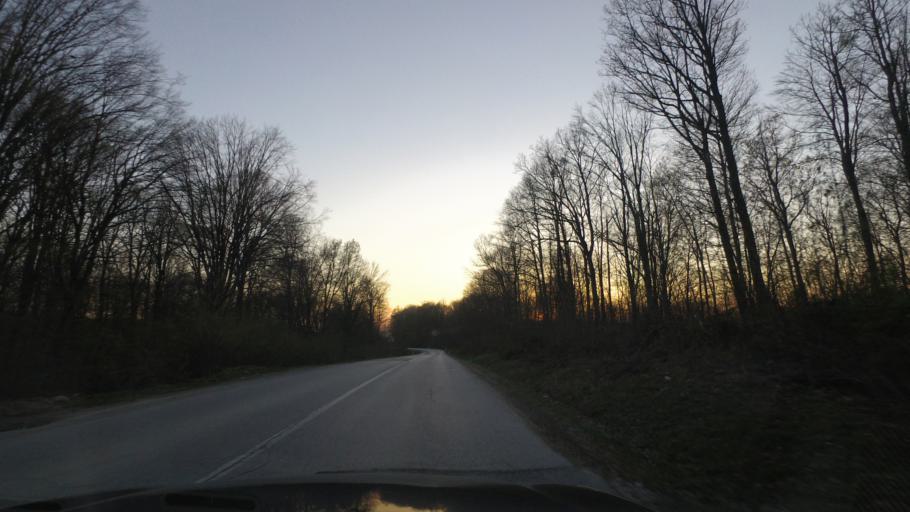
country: HR
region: Karlovacka
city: Vojnic
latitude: 45.3440
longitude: 15.7780
